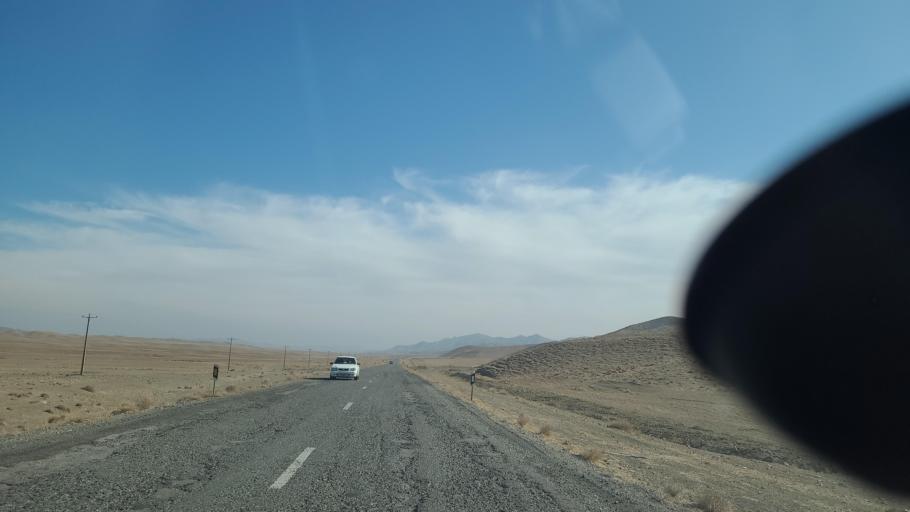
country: IR
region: Razavi Khorasan
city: Fariman
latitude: 35.5914
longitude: 59.6042
